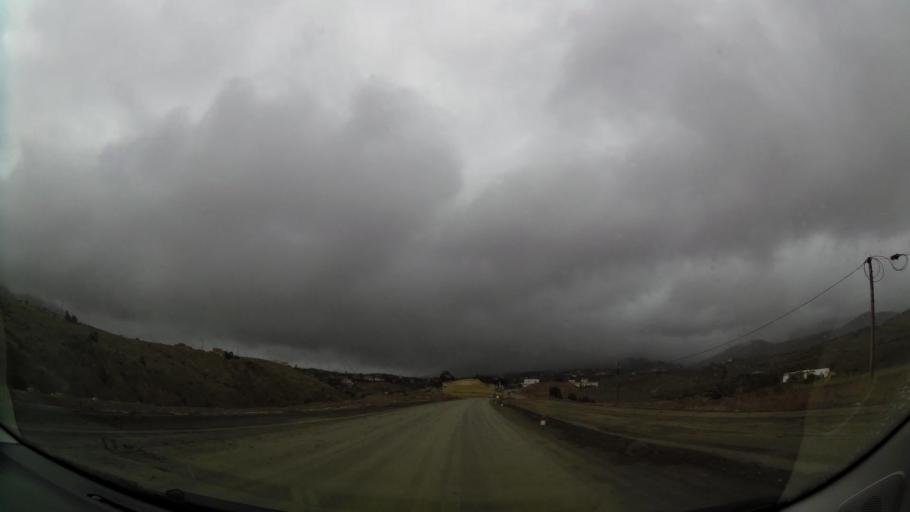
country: MA
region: Oriental
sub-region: Nador
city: Midar
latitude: 34.8937
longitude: -3.7659
